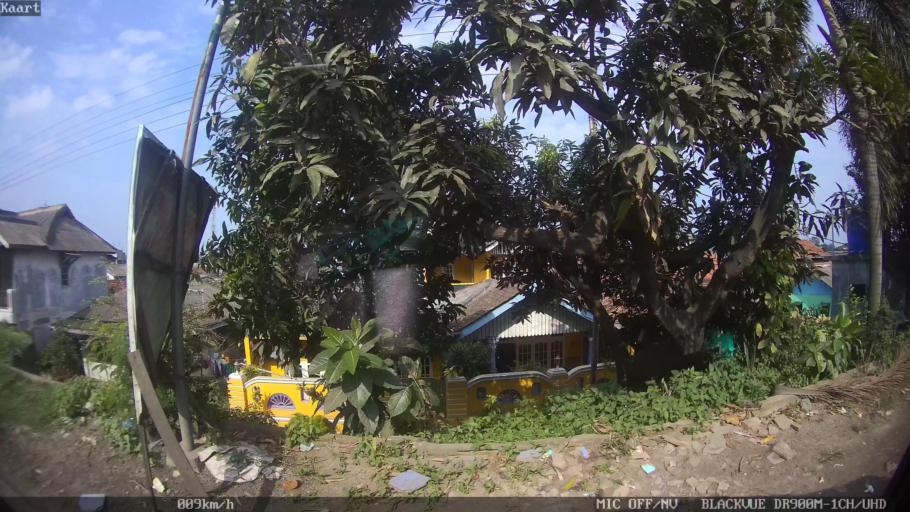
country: ID
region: Lampung
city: Panjang
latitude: -5.4682
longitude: 105.3231
